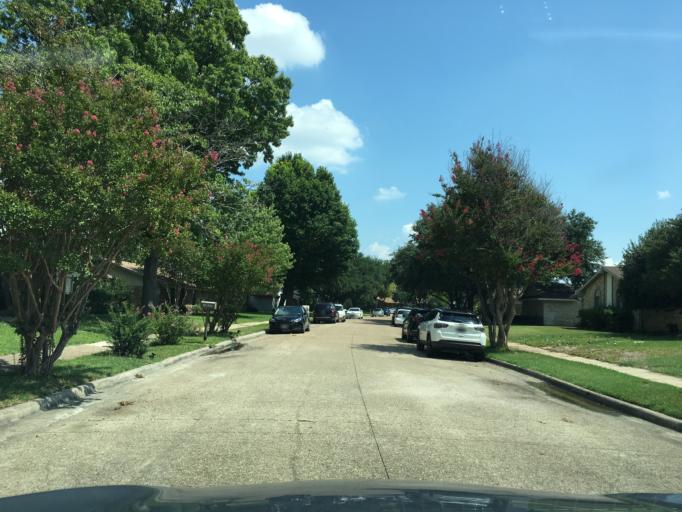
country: US
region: Texas
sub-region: Dallas County
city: Garland
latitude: 32.9404
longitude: -96.6601
